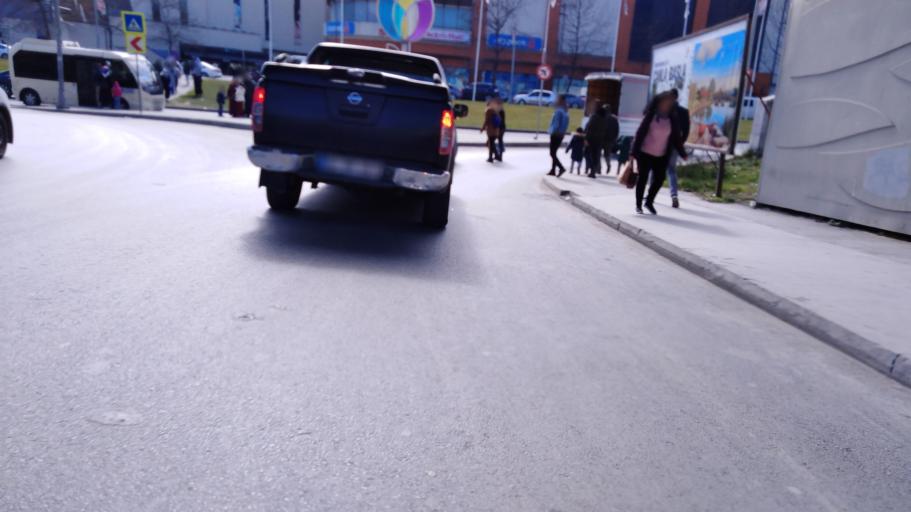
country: TR
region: Istanbul
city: Esenler
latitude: 41.0485
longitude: 28.8984
